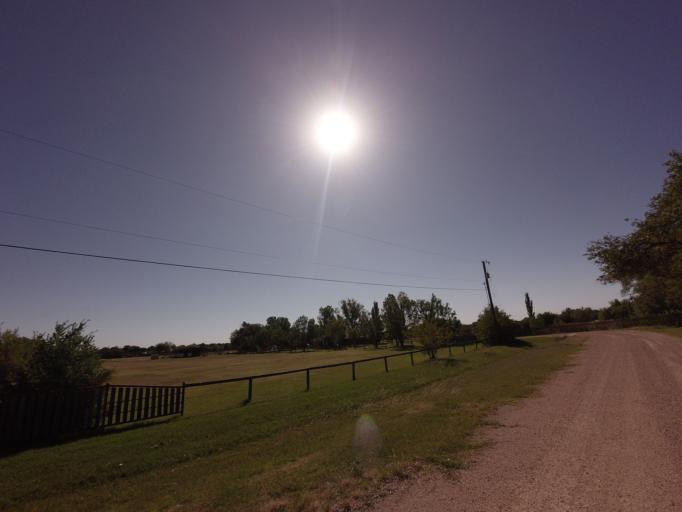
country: US
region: New Mexico
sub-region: Curry County
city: Clovis
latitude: 34.4314
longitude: -103.1876
